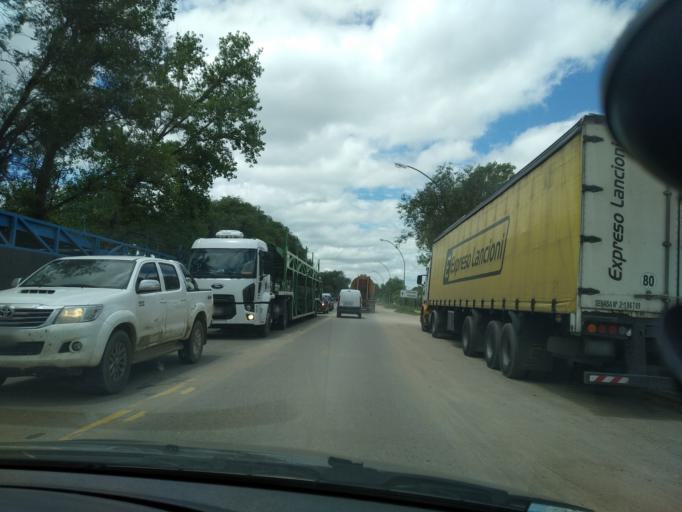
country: AR
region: Cordoba
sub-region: Departamento de Rio Segundo
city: Rio Segundo
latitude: -31.6469
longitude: -63.9047
